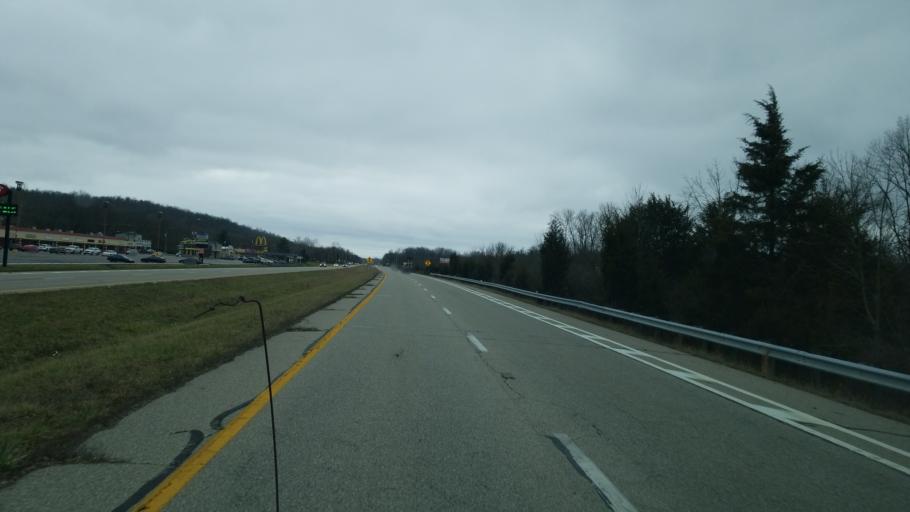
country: US
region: Ohio
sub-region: Clermont County
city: New Richmond
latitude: 38.9706
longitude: -84.2888
